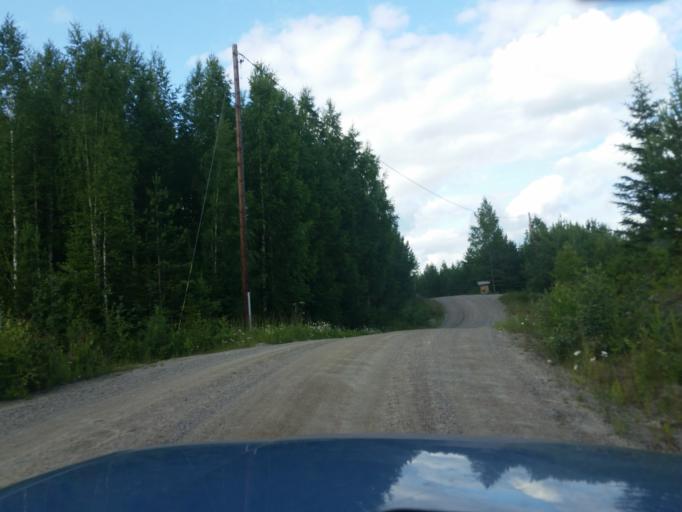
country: FI
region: Southern Savonia
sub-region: Savonlinna
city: Sulkava
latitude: 61.6925
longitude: 28.2906
